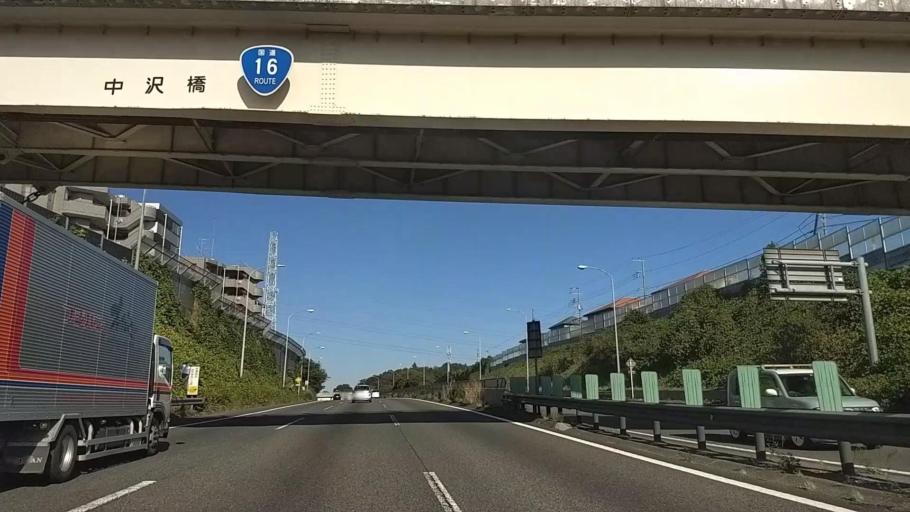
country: JP
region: Kanagawa
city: Minami-rinkan
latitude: 35.4700
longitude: 139.5330
